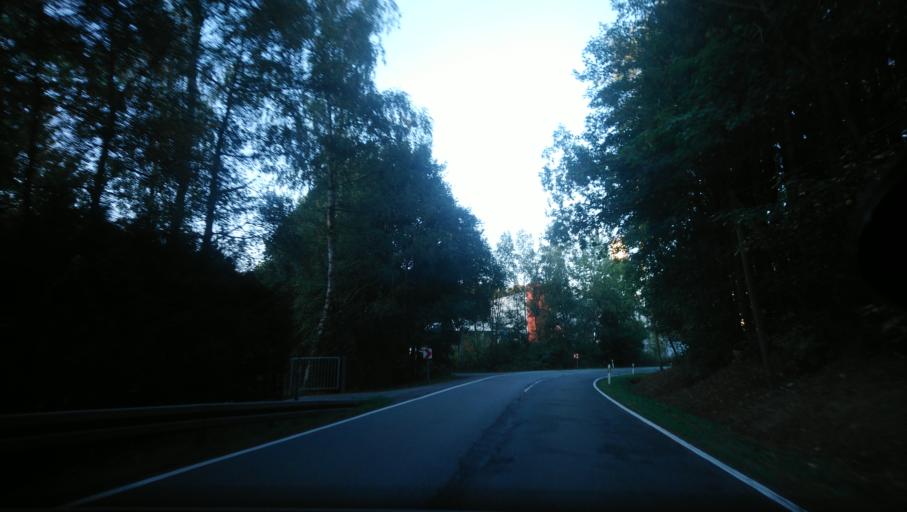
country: DE
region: Saxony
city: Wiesa
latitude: 50.6050
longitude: 12.9864
